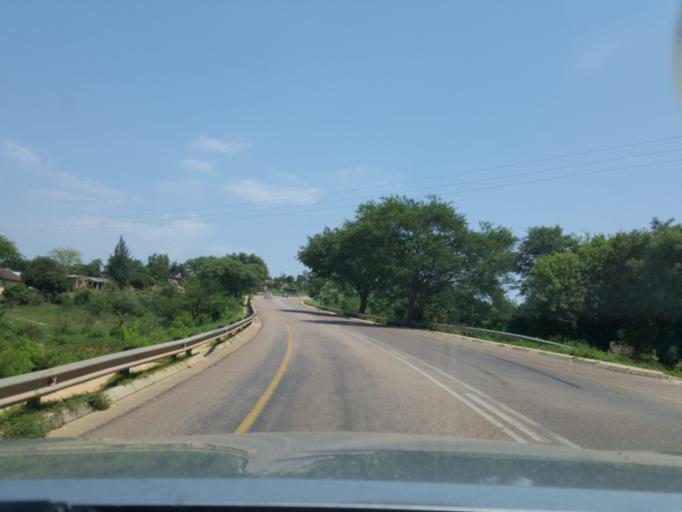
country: ZA
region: Mpumalanga
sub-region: Ehlanzeni District
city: Graksop
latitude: -24.9845
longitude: 31.1097
